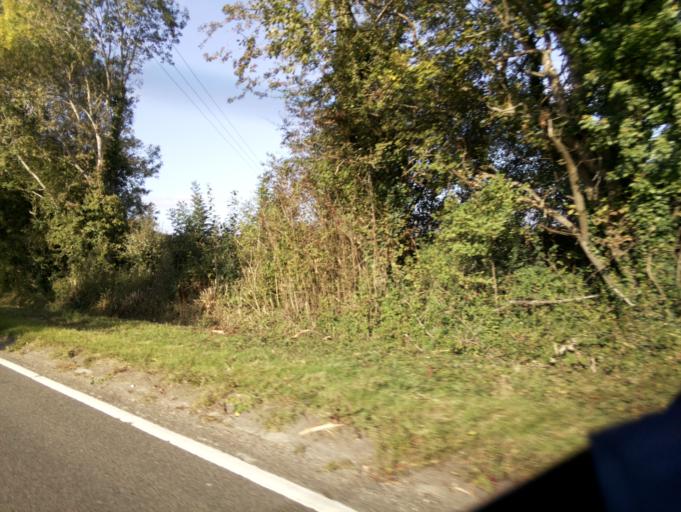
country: GB
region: England
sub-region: Hampshire
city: Alton
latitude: 51.1310
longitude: -0.9940
